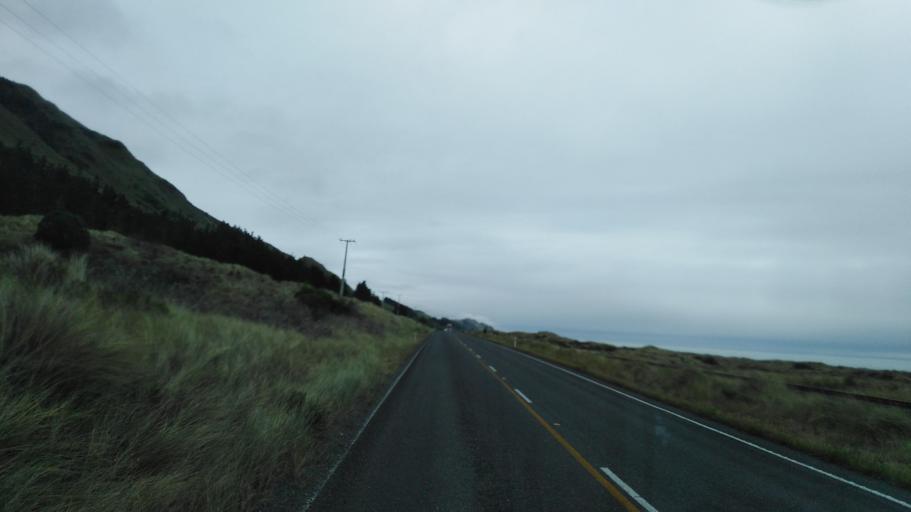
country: NZ
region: Canterbury
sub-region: Kaikoura District
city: Kaikoura
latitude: -42.0487
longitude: 173.9621
